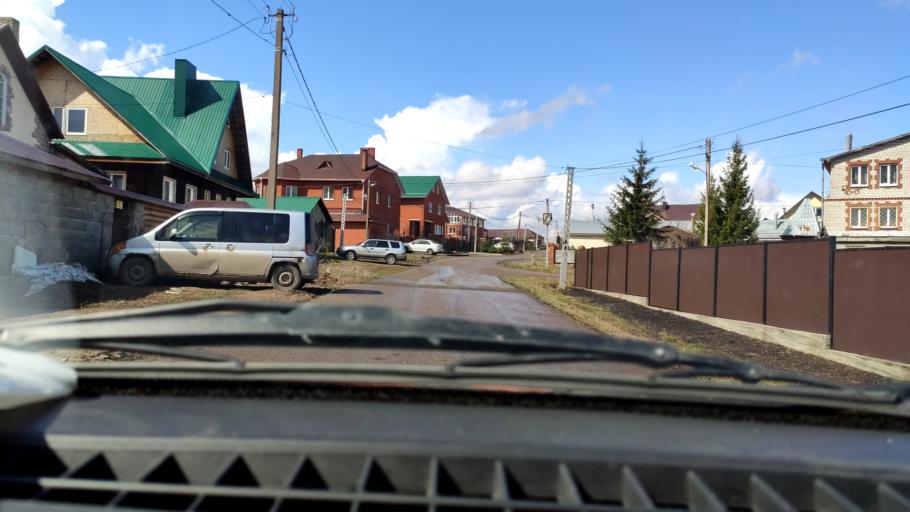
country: RU
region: Bashkortostan
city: Mikhaylovka
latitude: 54.8298
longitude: 55.9110
